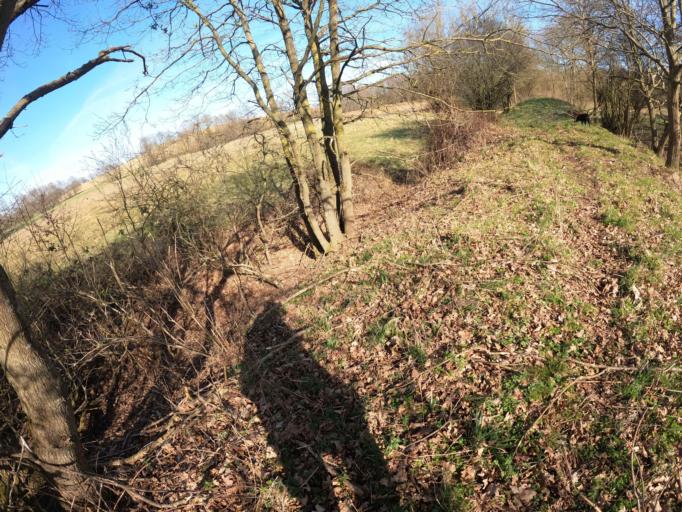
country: PL
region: West Pomeranian Voivodeship
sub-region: Powiat gryficki
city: Brojce
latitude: 53.9230
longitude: 15.3056
